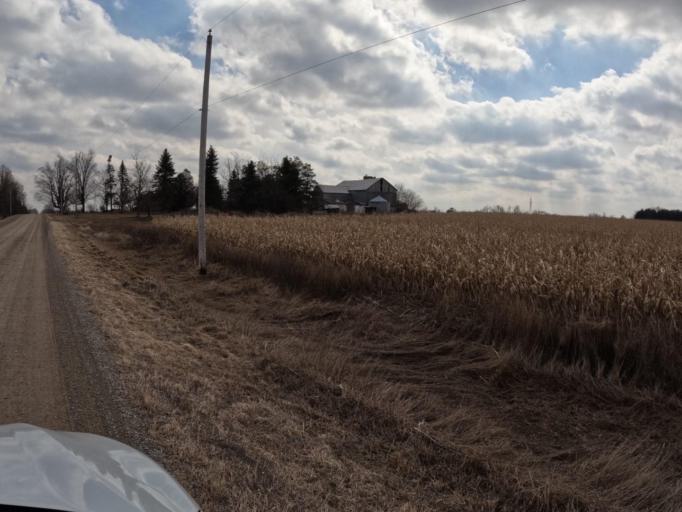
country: CA
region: Ontario
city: Shelburne
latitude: 43.9629
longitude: -80.2823
